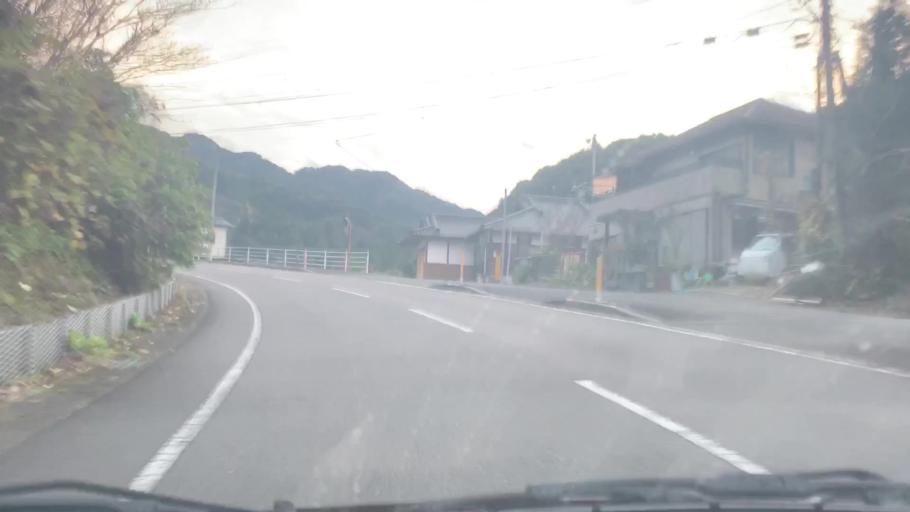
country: JP
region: Saga Prefecture
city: Kashima
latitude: 33.0211
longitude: 130.0670
